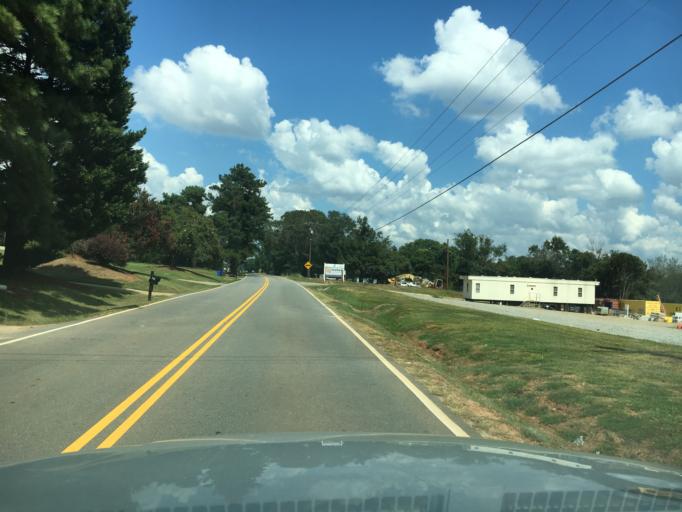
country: US
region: South Carolina
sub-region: Spartanburg County
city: Roebuck
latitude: 34.9034
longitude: -82.0062
